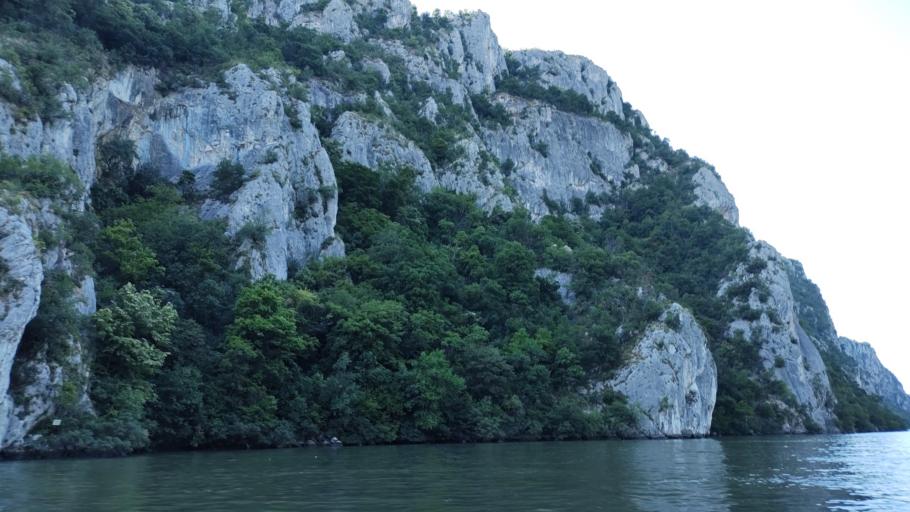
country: RO
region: Mehedinti
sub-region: Comuna Dubova
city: Dubova
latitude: 44.5914
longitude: 22.2598
